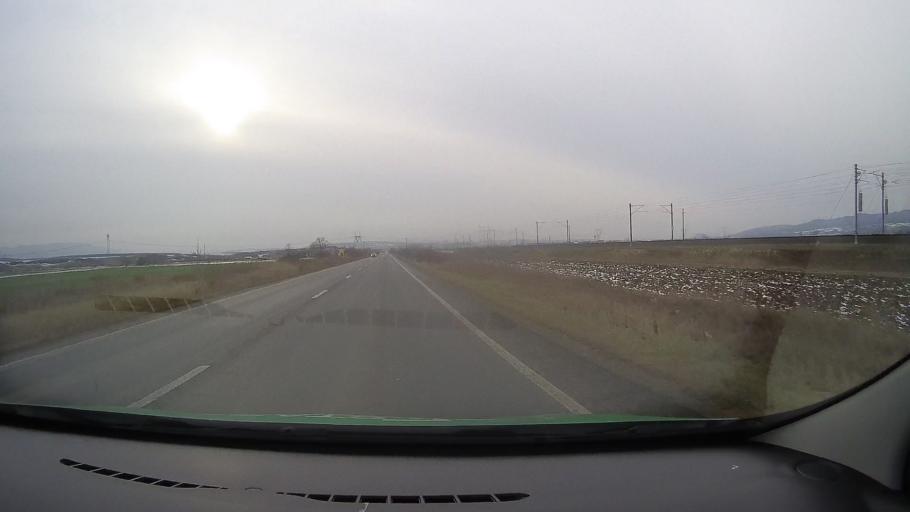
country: RO
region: Hunedoara
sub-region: Comuna Geoagiu
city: Geoagiu
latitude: 45.8787
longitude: 23.2417
